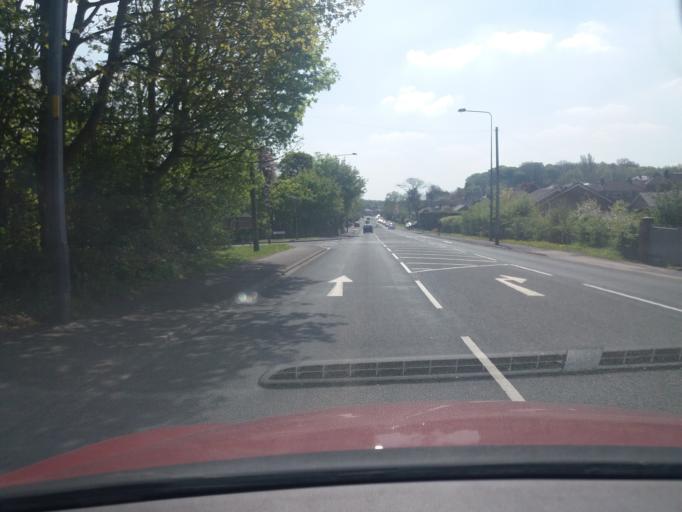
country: GB
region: England
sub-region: Lancashire
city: Clayton-le-Woods
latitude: 53.6986
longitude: -2.6392
